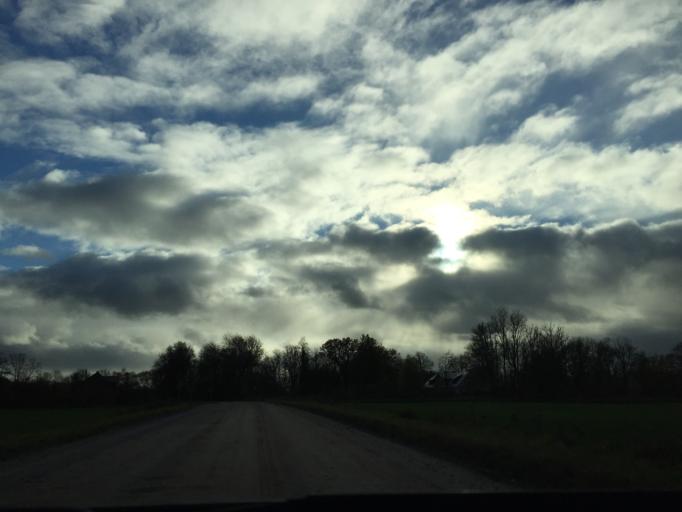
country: LV
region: Jaunpils
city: Jaunpils
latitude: 56.9261
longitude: 22.9494
